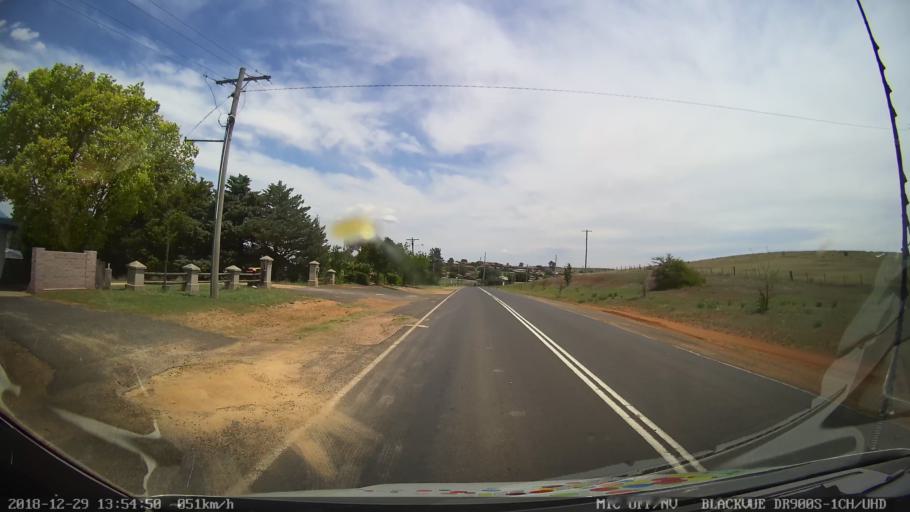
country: AU
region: New South Wales
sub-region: Cooma-Monaro
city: Cooma
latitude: -36.2165
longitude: 149.1505
